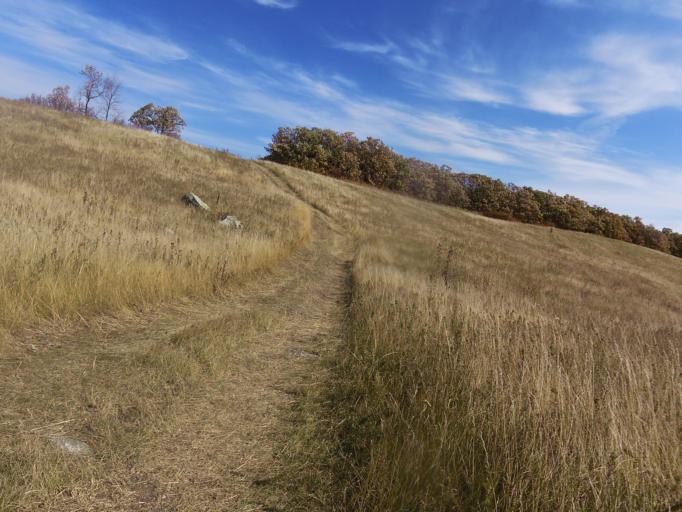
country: CA
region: Manitoba
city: Morden
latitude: 48.9487
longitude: -98.0654
